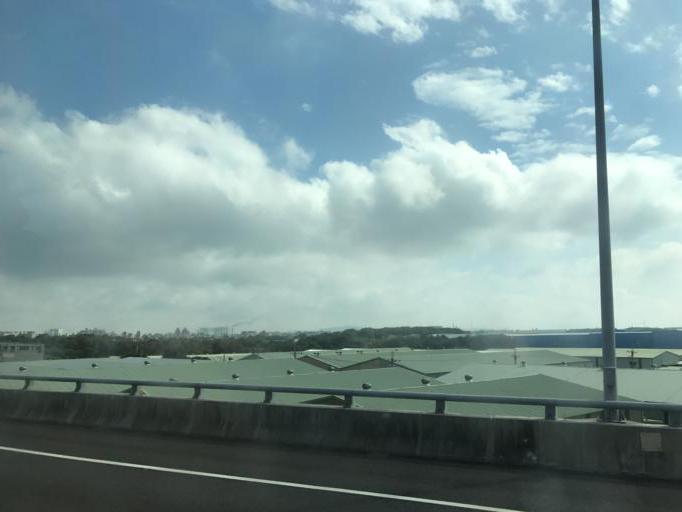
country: TW
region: Taiwan
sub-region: Taoyuan
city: Taoyuan
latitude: 25.0653
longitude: 121.3472
